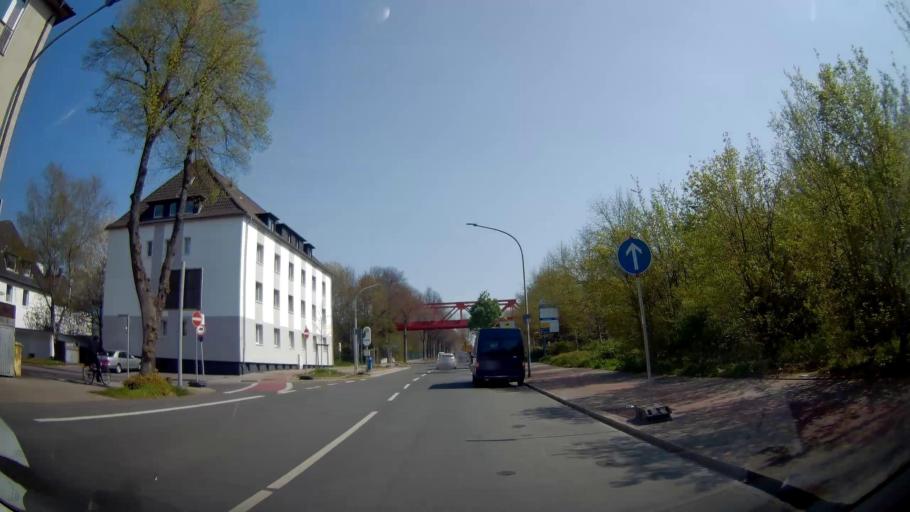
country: DE
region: North Rhine-Westphalia
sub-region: Regierungsbezirk Munster
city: Gelsenkirchen
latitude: 51.5333
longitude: 7.1115
